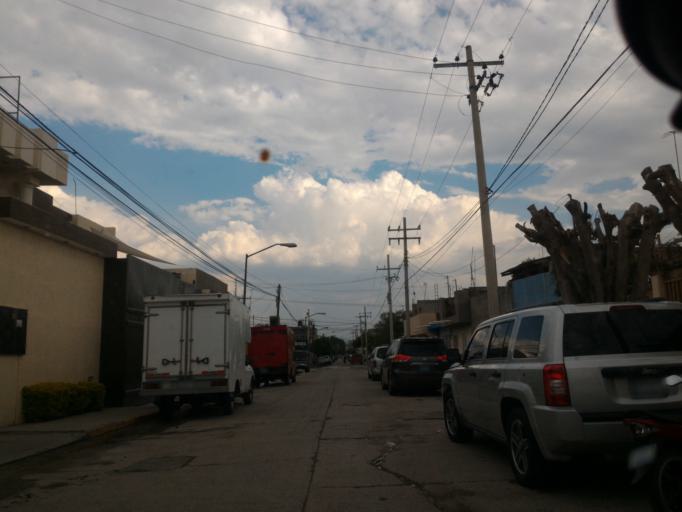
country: MX
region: Guanajuato
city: San Francisco del Rincon
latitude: 21.0335
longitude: -101.8579
